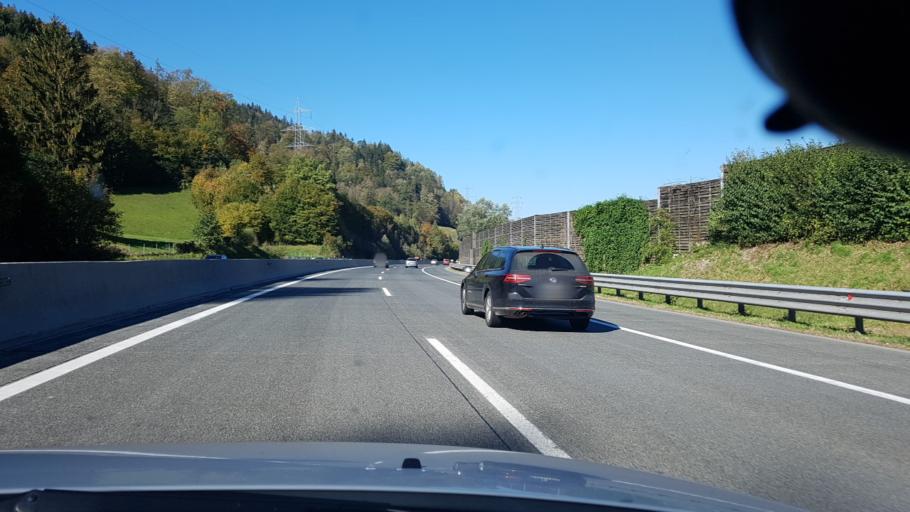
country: AT
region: Salzburg
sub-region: Politischer Bezirk Hallein
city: Kuchl
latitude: 47.6135
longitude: 13.1401
